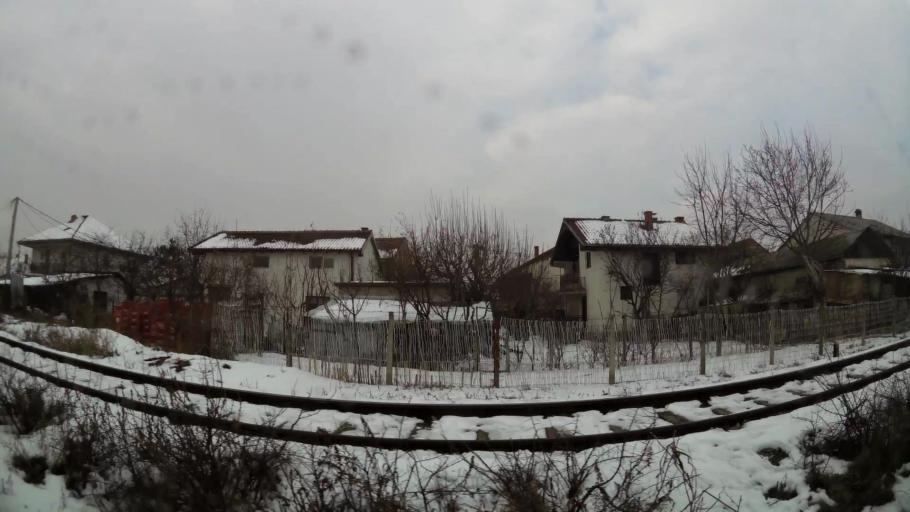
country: MK
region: Saraj
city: Saraj
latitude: 42.0370
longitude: 21.3514
